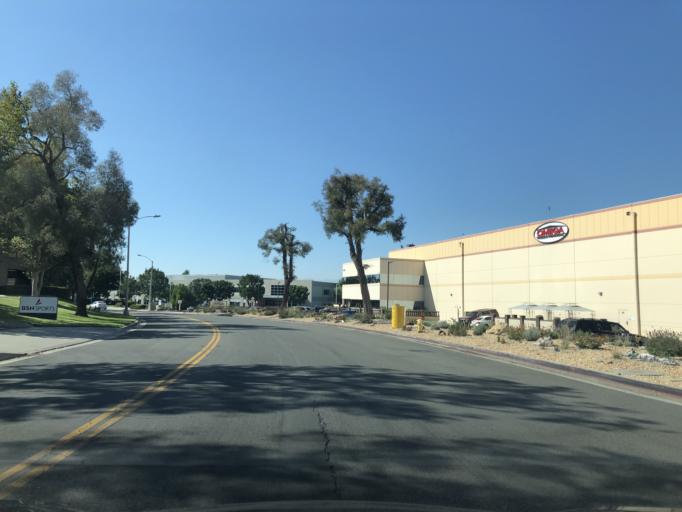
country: US
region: California
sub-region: Riverside County
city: Home Gardens
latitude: 33.8605
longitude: -117.5390
